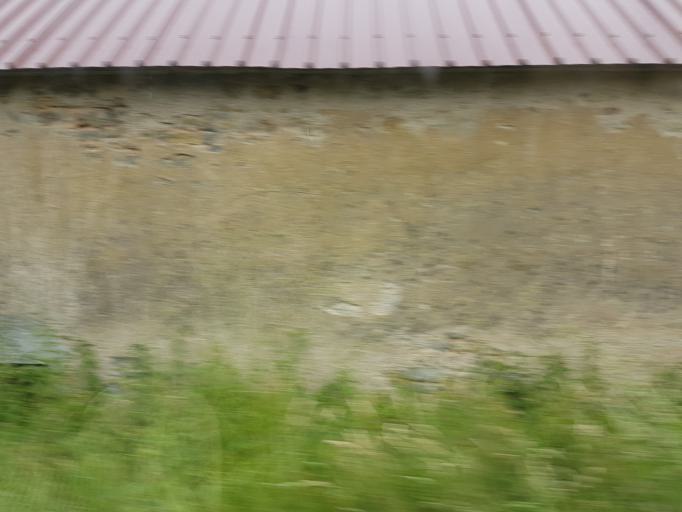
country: FR
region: Bourgogne
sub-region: Departement de la Nievre
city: Corbigny
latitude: 47.2003
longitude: 3.7234
